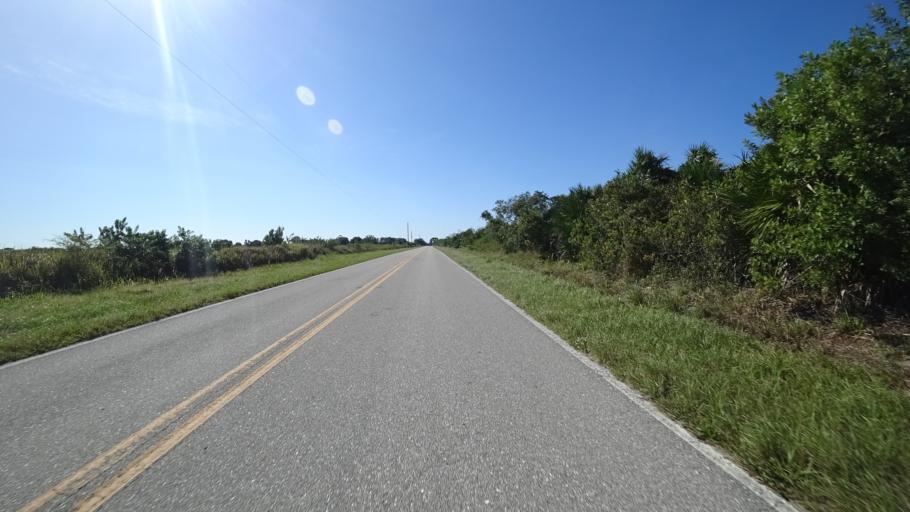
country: US
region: Florida
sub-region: Hillsborough County
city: Wimauma
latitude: 27.6085
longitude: -82.2927
